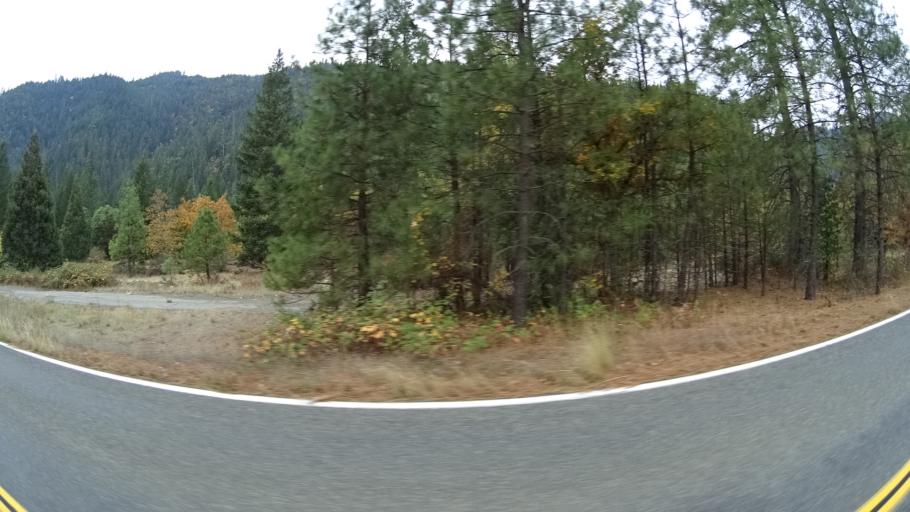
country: US
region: California
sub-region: Siskiyou County
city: Happy Camp
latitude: 41.8787
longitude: -123.4200
